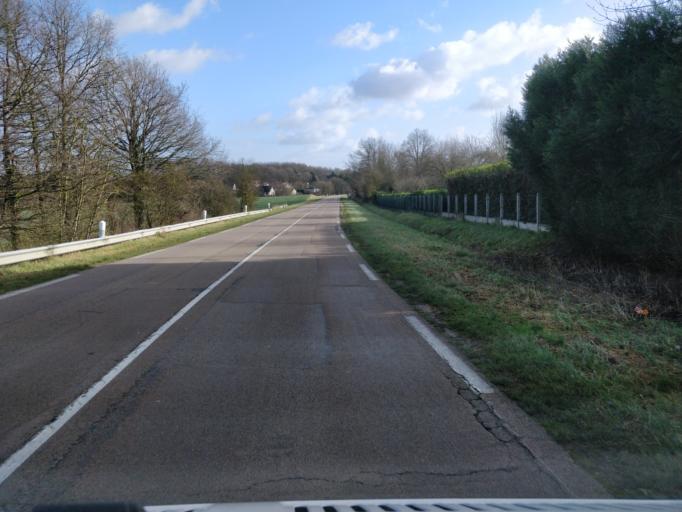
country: FR
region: Bourgogne
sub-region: Departement de l'Yonne
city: Cheroy
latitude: 48.2030
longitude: 3.0051
